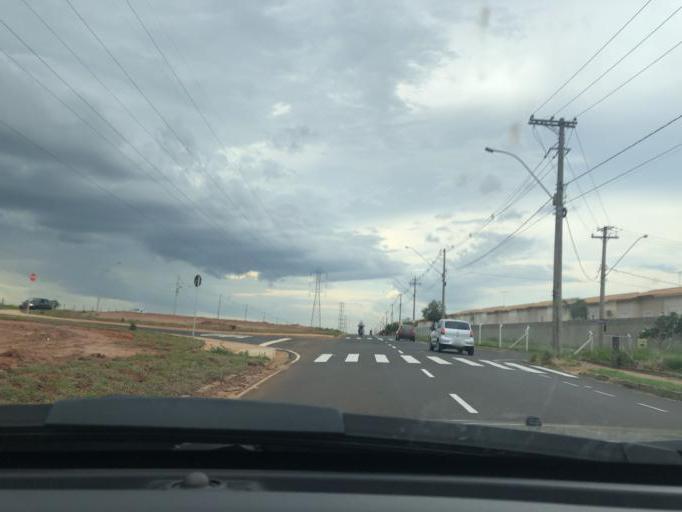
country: BR
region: Sao Paulo
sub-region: Sao Jose Do Rio Preto
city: Sao Jose do Rio Preto
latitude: -20.8402
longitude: -49.4164
